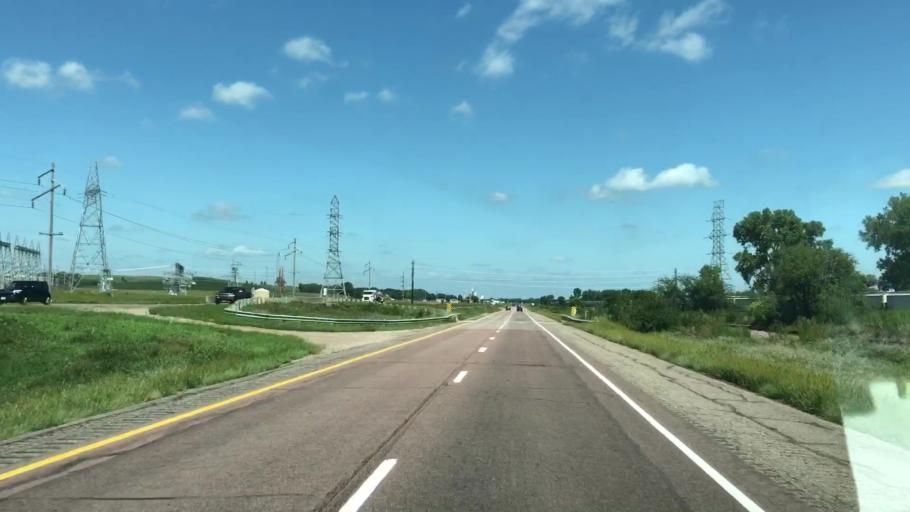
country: US
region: Iowa
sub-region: Woodbury County
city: Sioux City
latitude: 42.5970
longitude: -96.3035
